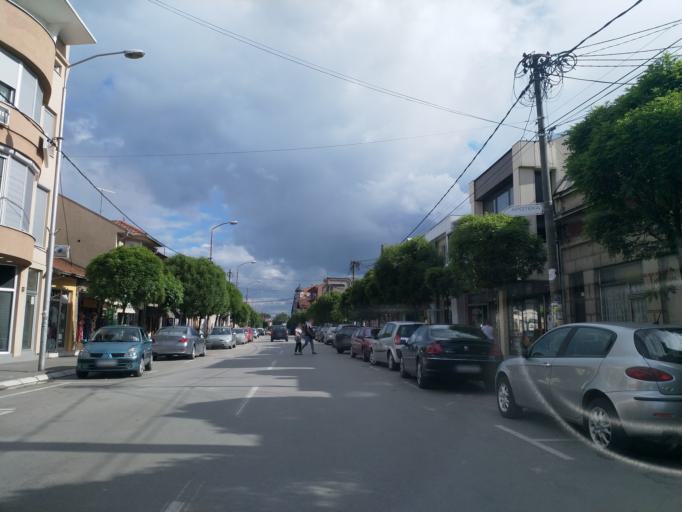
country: RS
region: Central Serbia
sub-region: Pomoravski Okrug
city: Paracin
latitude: 43.8577
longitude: 21.4116
